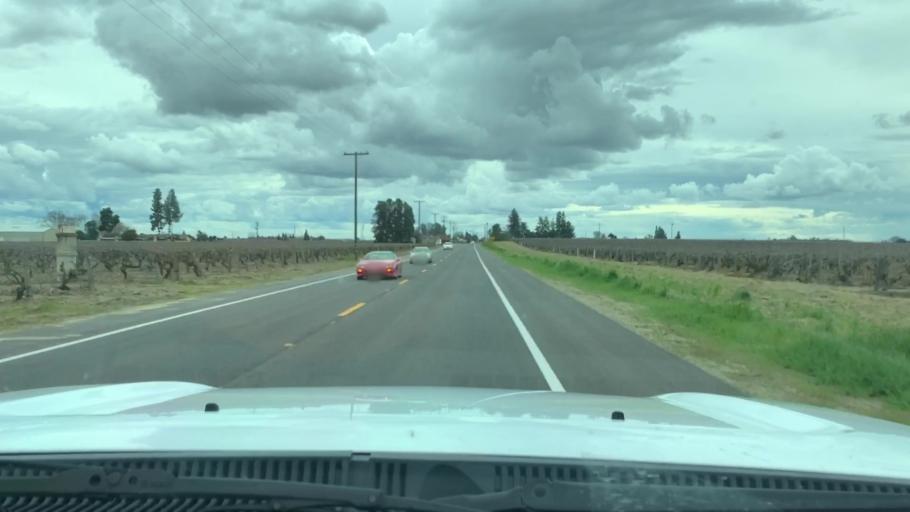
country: US
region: California
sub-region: Fresno County
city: Fowler
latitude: 36.5650
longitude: -119.6825
